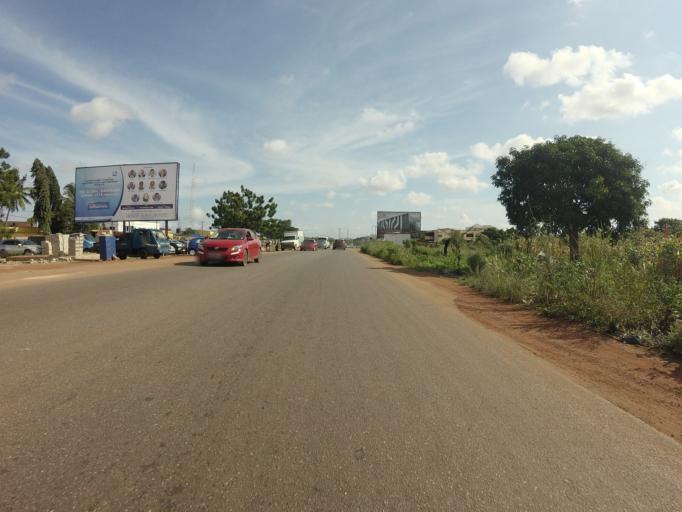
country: GH
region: Greater Accra
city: Medina Estates
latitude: 5.6481
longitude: -0.1694
